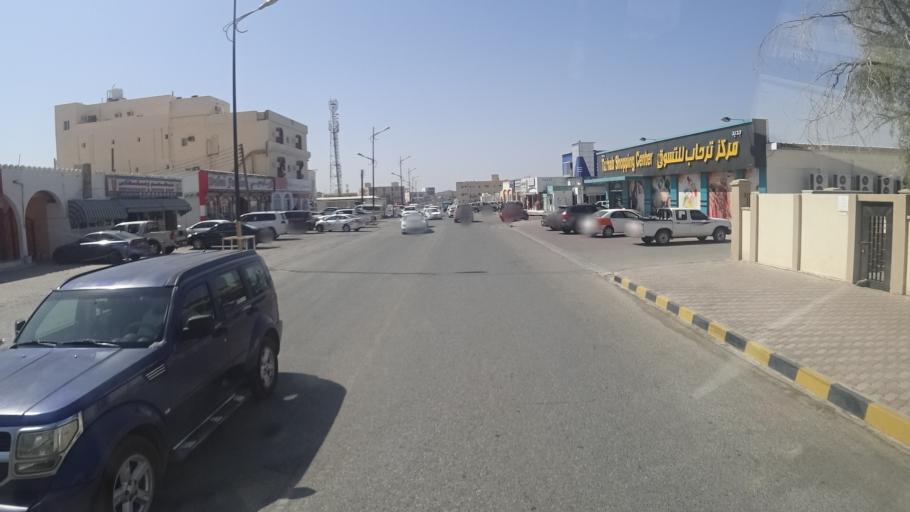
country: OM
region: Ash Sharqiyah
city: Ibra'
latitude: 22.6942
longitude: 58.5453
